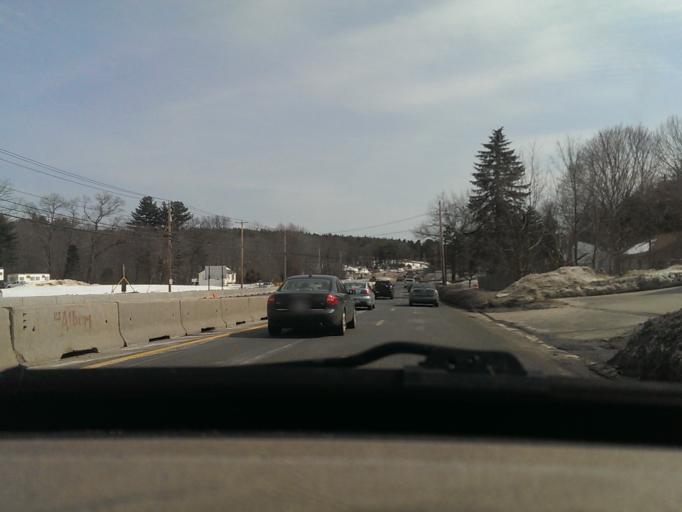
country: US
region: Massachusetts
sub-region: Worcester County
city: Sutton
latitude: 42.1595
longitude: -71.7353
